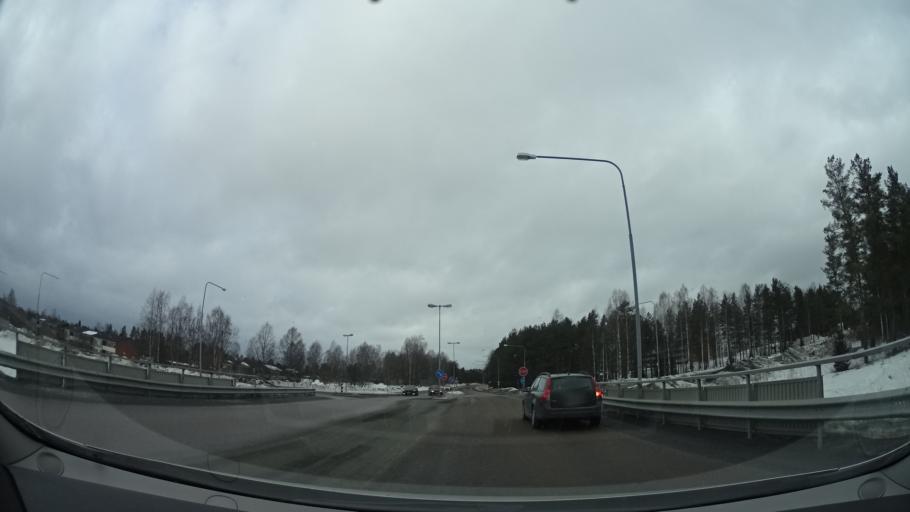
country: SE
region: Vaesterbotten
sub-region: Skelleftea Kommun
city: Skelleftea
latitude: 64.7501
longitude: 21.0193
